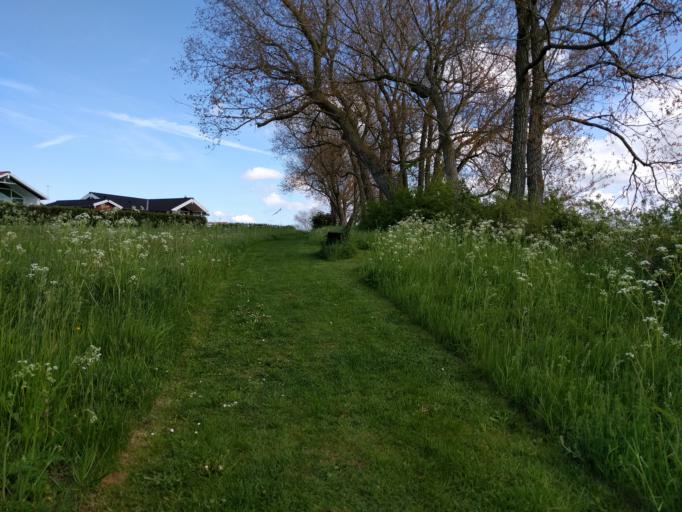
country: DK
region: Zealand
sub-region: Guldborgsund Kommune
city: Stubbekobing
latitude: 54.9159
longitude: 12.0571
